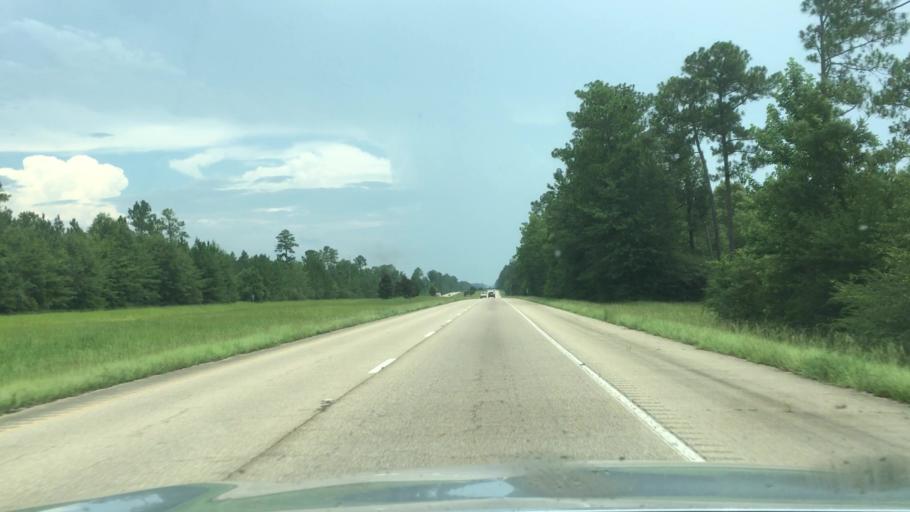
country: US
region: Mississippi
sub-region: Lamar County
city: Lumberton
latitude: 30.9664
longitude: -89.4360
